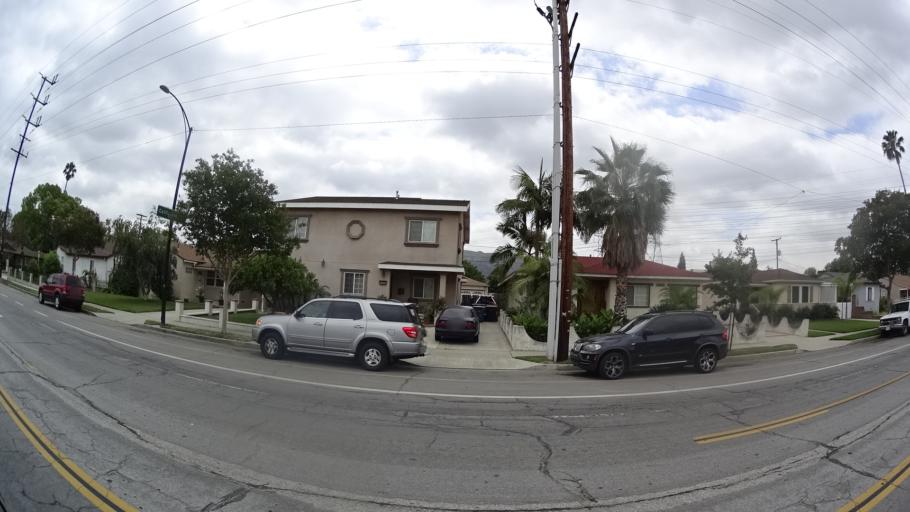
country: US
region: California
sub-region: Los Angeles County
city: Universal City
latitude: 34.1622
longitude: -118.3401
